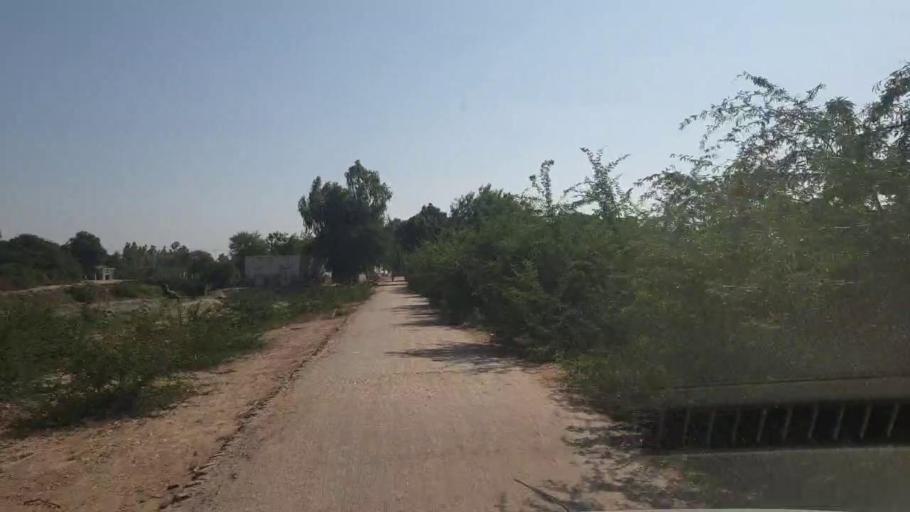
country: PK
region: Sindh
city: Tando Bago
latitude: 24.7572
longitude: 69.1549
